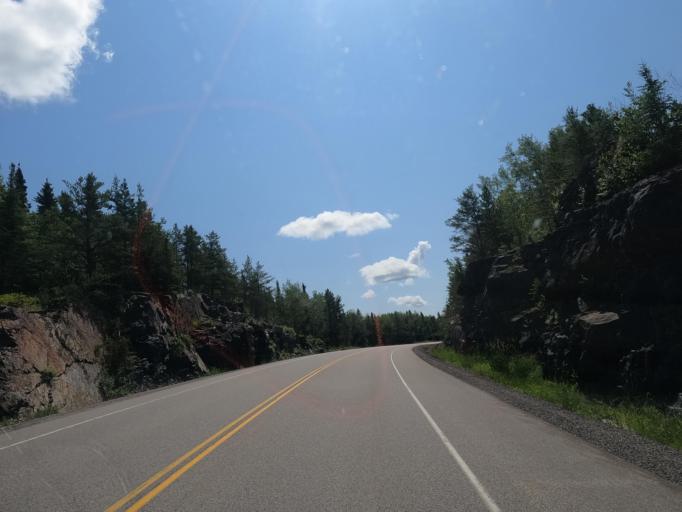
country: CA
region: Ontario
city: Dryden
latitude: 49.8864
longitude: -93.3603
